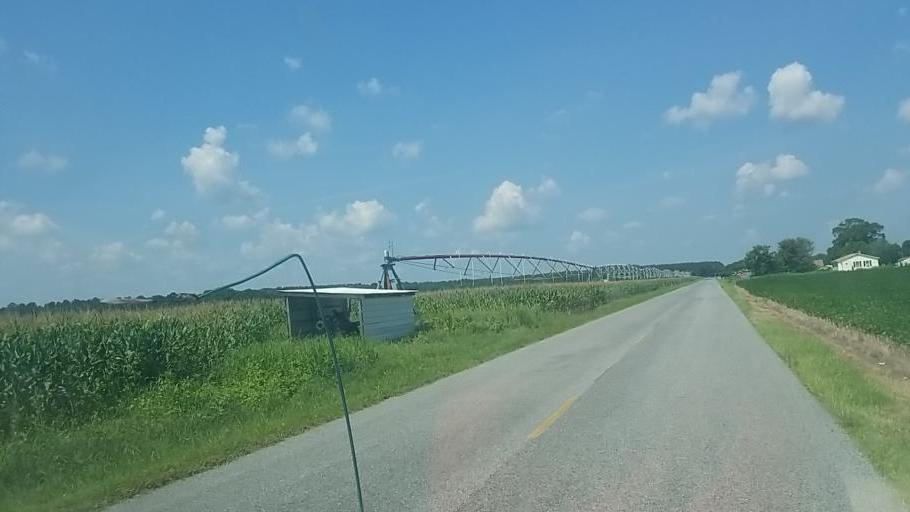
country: US
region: Maryland
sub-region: Worcester County
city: Berlin
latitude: 38.2952
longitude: -75.2571
